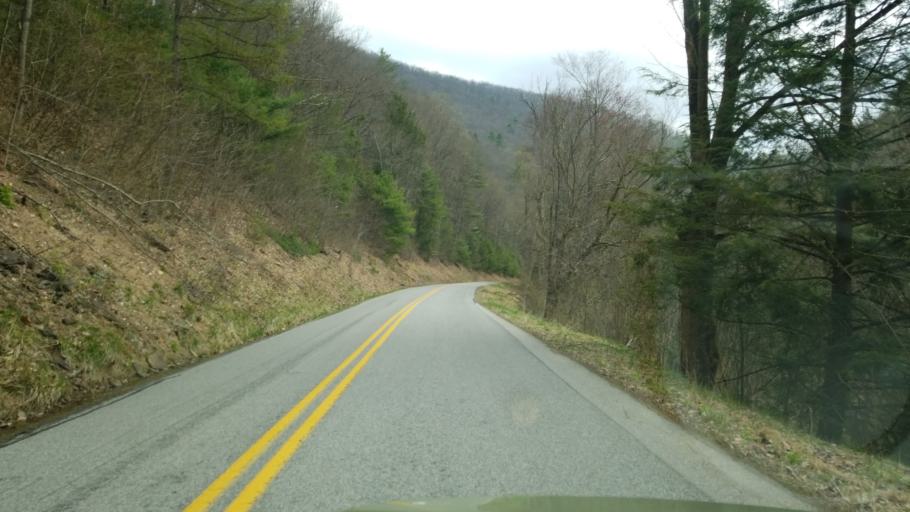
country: US
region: Pennsylvania
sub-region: Cameron County
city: Emporium
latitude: 41.2803
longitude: -78.1389
